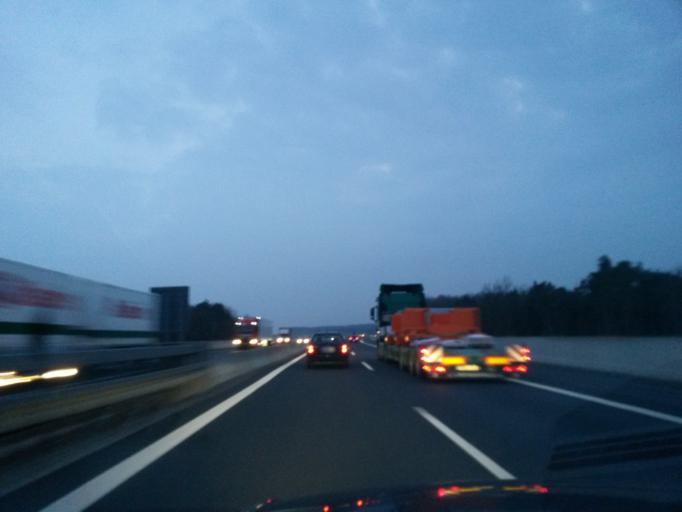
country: DE
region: Bavaria
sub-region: Regierungsbezirk Unterfranken
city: Rannungen
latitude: 50.1943
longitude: 10.2110
